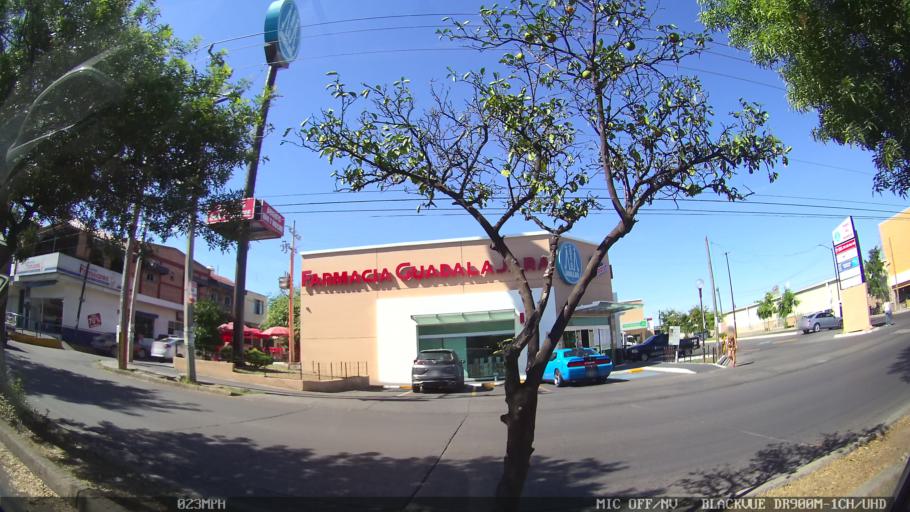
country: MX
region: Jalisco
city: Tlaquepaque
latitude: 20.6794
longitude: -103.2875
